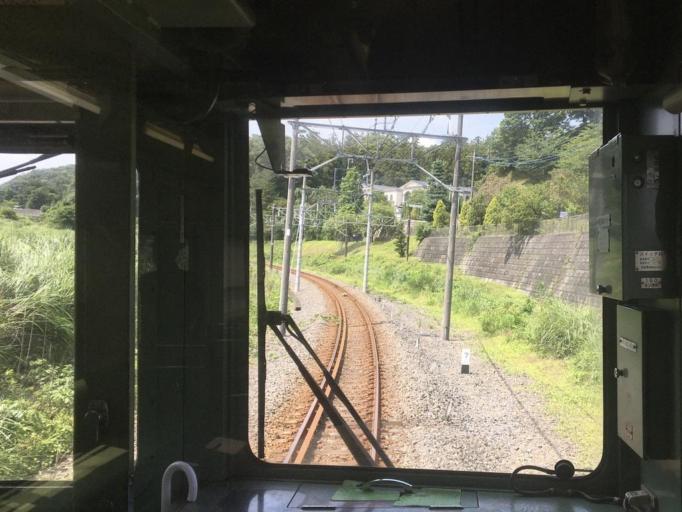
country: JP
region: Tochigi
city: Tanuma
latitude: 36.3966
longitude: 139.6045
